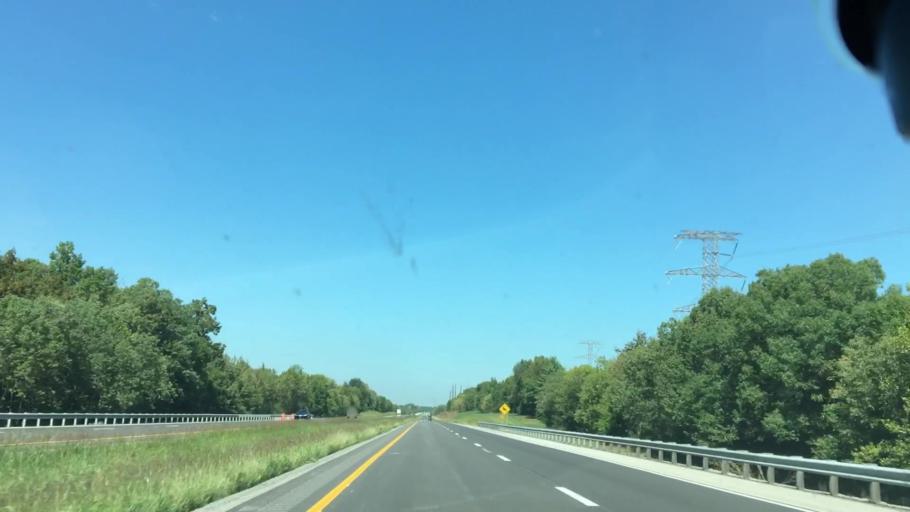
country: US
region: Kentucky
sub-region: Webster County
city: Sebree
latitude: 37.6309
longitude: -87.5089
